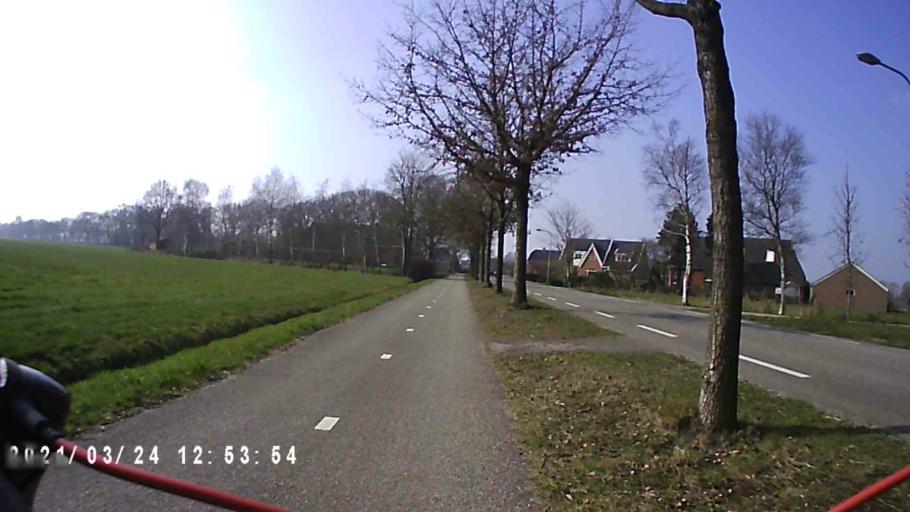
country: NL
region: Groningen
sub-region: Gemeente Leek
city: Leek
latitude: 53.1556
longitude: 6.3173
